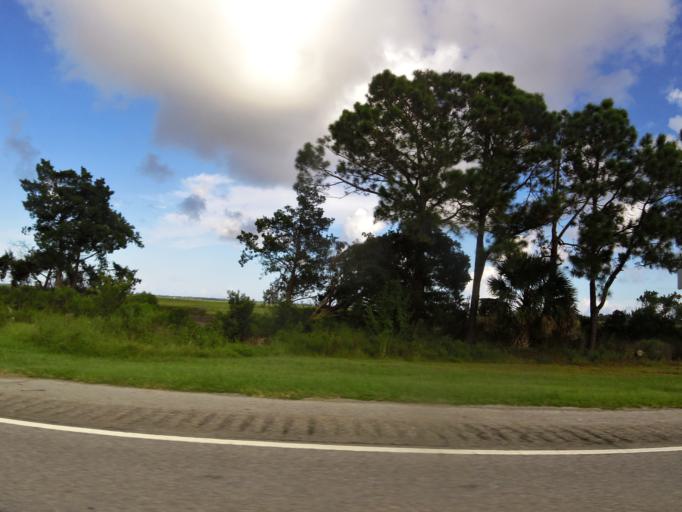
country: US
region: Georgia
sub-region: Glynn County
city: Country Club Estates
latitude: 31.1840
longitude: -81.4703
